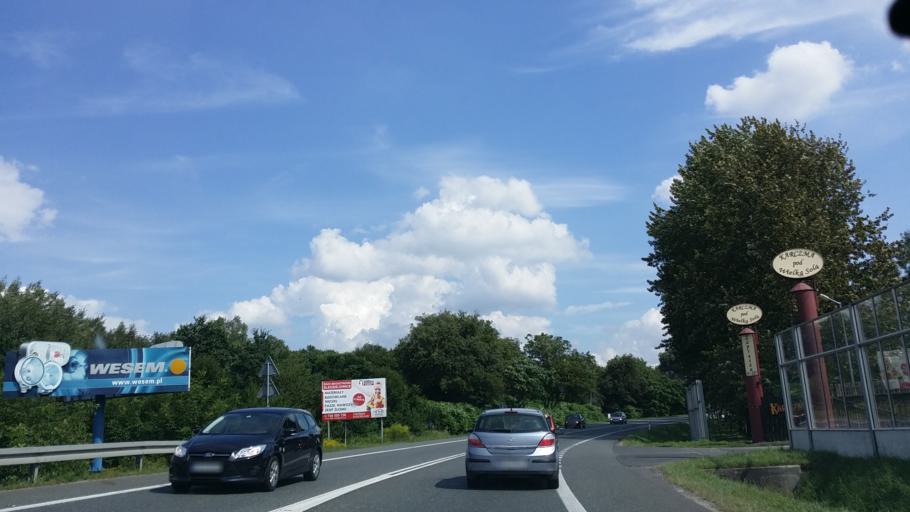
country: PL
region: Lesser Poland Voivodeship
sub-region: Powiat wielicki
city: Wieliczka
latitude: 49.9939
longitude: 20.0767
